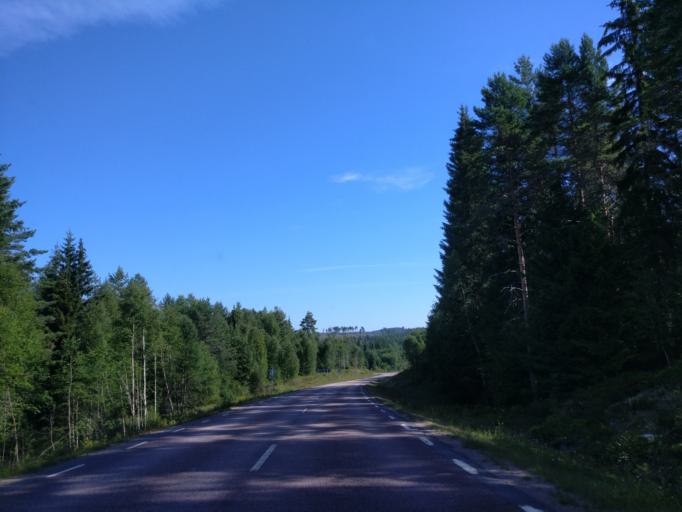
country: SE
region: Vaermland
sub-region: Hagfors Kommun
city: Hagfors
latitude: 60.0238
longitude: 13.9039
